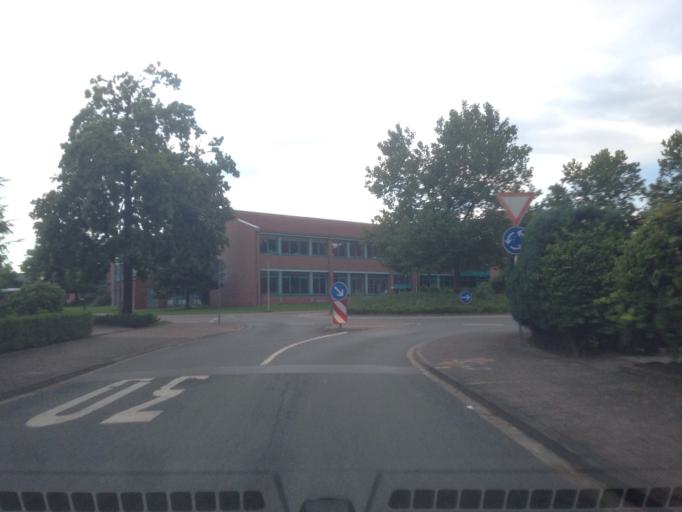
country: DE
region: North Rhine-Westphalia
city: Olfen
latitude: 51.7155
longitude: 7.3767
